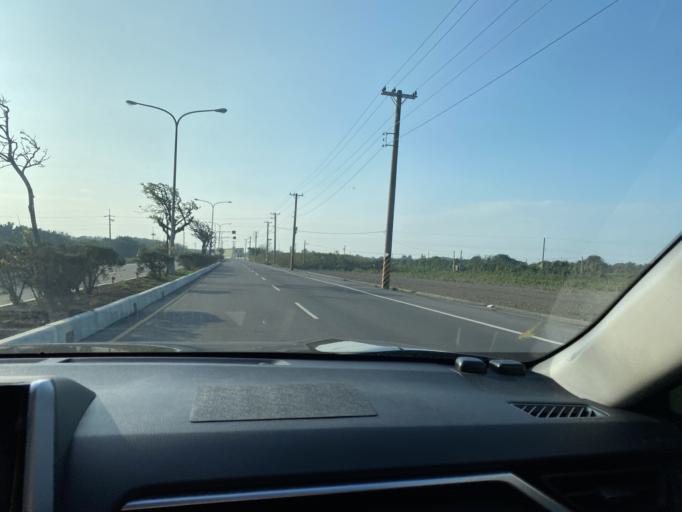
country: TW
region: Taiwan
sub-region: Changhua
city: Chang-hua
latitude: 23.9614
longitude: 120.3579
